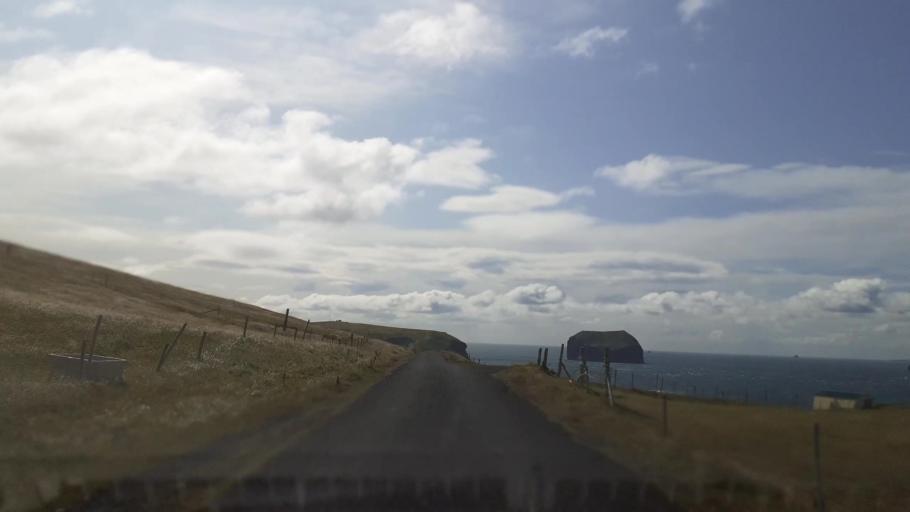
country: IS
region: South
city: Vestmannaeyjar
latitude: 63.4194
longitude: -20.2806
